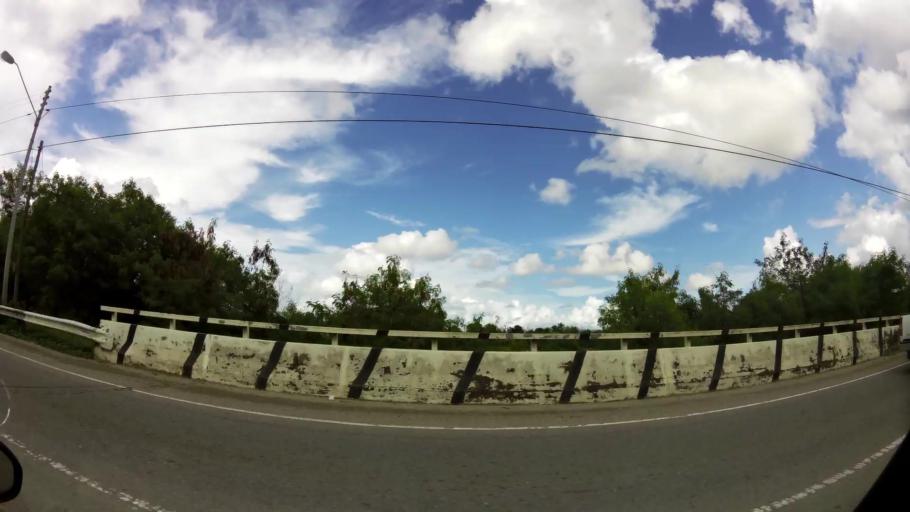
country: TT
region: City of San Fernando
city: Mon Repos
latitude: 10.2623
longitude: -61.4489
